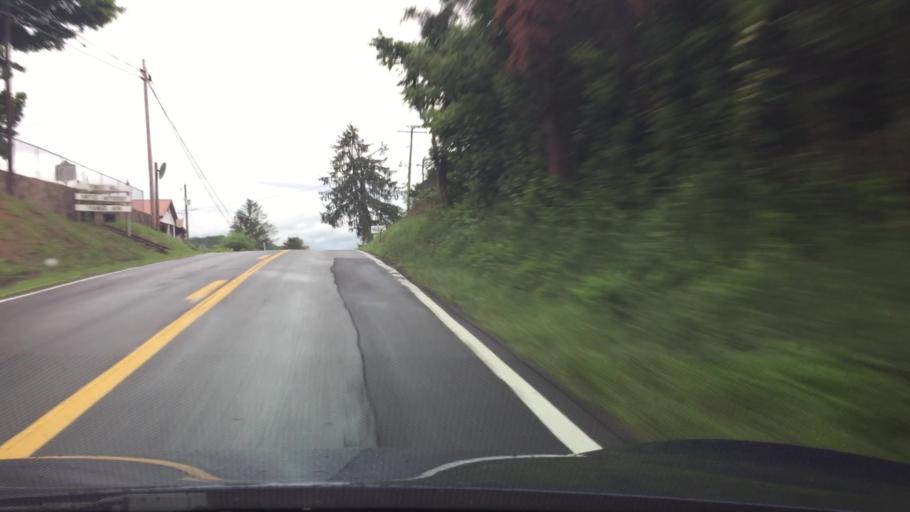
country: US
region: West Virginia
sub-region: Summers County
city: Hinton
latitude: 37.5707
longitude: -80.7893
